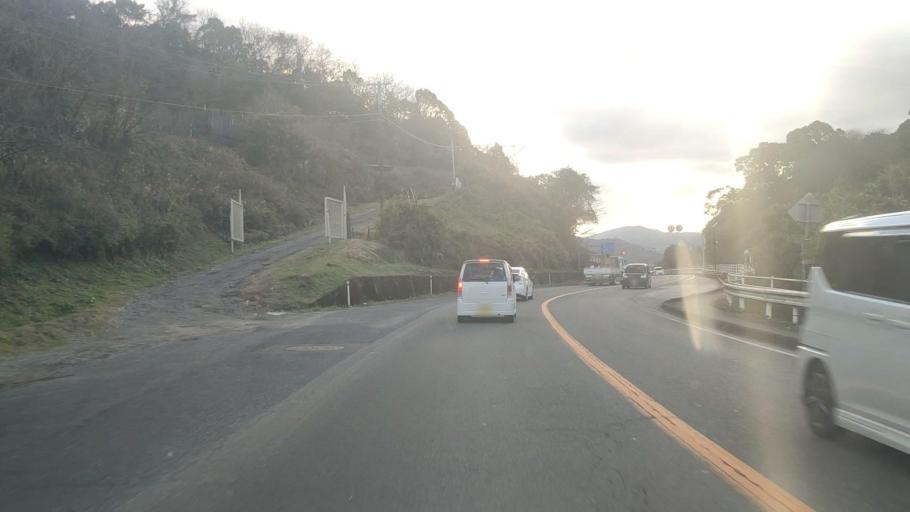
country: JP
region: Saga Prefecture
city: Saga-shi
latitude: 33.2897
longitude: 130.1681
